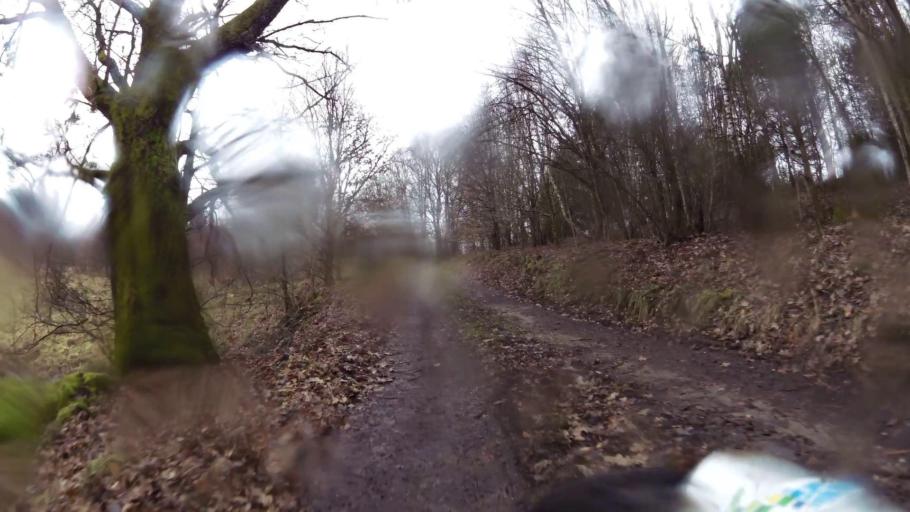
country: PL
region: Pomeranian Voivodeship
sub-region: Powiat bytowski
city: Miastko
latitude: 54.0406
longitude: 17.0414
